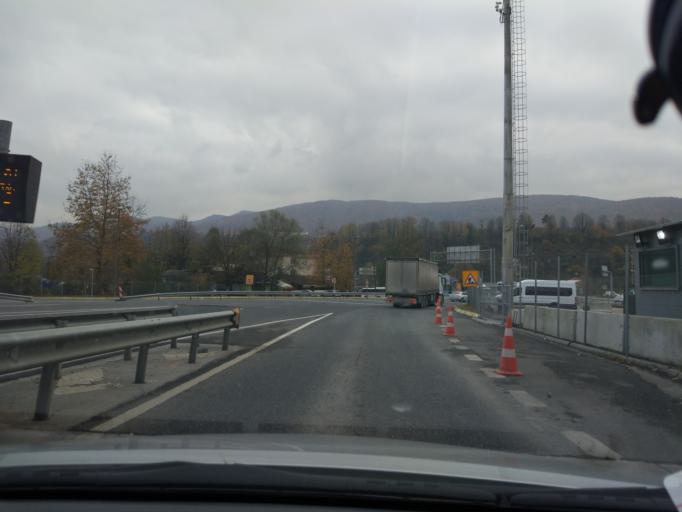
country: TR
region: Duzce
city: Kaynasli
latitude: 40.7838
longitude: 31.2776
